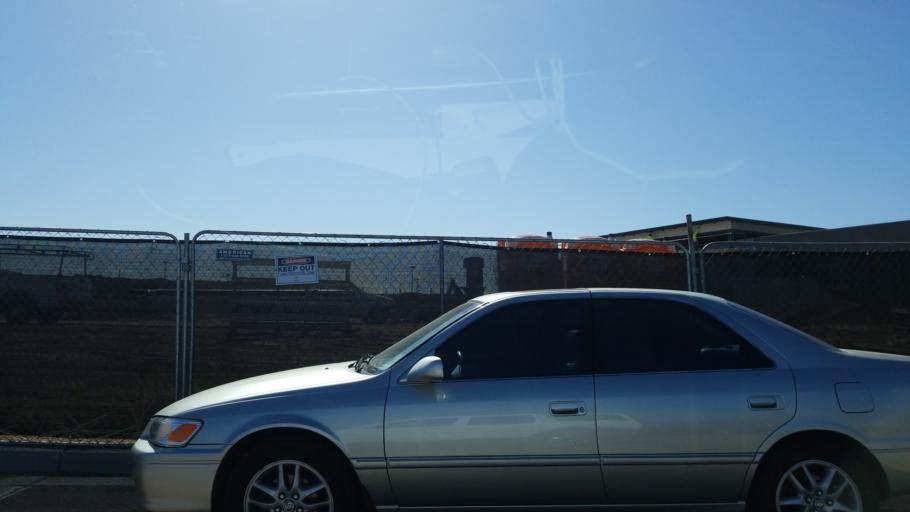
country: US
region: Arizona
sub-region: Maricopa County
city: Scottsdale
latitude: 33.5121
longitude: -111.8797
